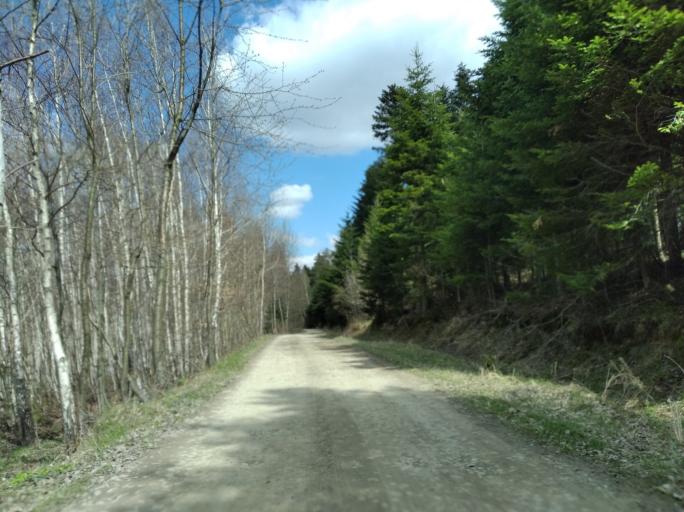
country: PL
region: Subcarpathian Voivodeship
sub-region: Powiat strzyzowski
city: Wysoka Strzyzowska
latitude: 49.8278
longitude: 21.7701
